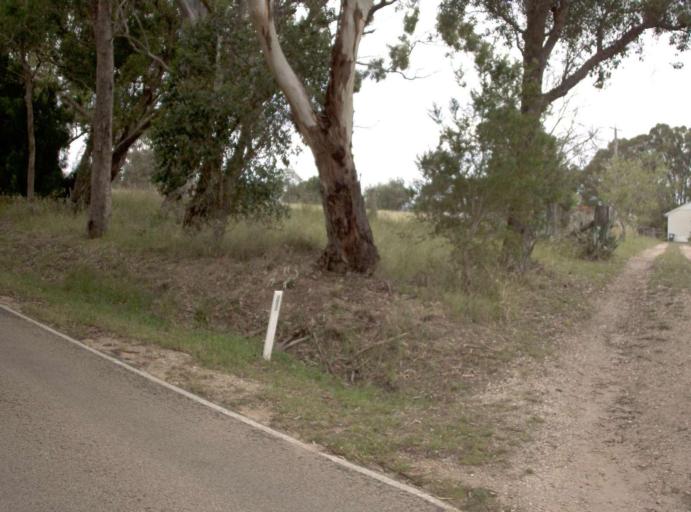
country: AU
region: Victoria
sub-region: East Gippsland
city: Bairnsdale
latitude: -37.7919
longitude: 147.6073
